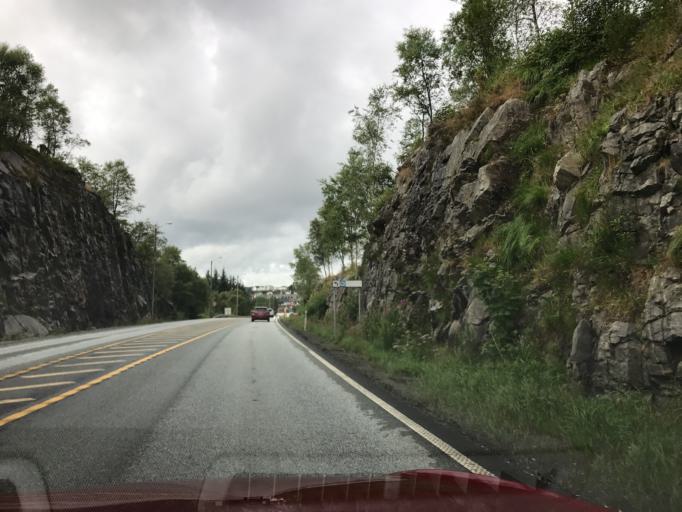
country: NO
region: Rogaland
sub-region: Tysvaer
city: Aksdal
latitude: 59.4191
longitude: 5.4114
